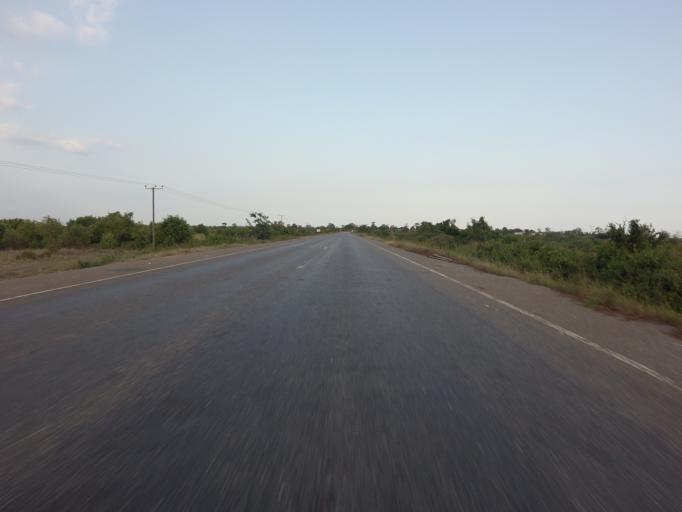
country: GH
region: Volta
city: Anloga
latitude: 6.0764
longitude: 0.5993
